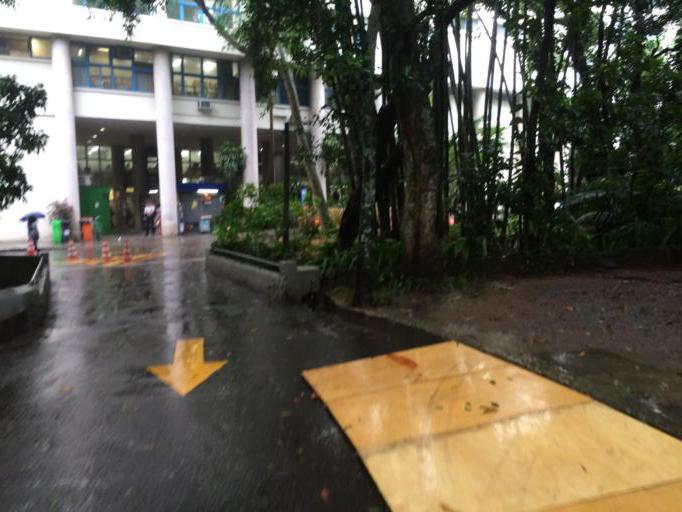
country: BR
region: Rio de Janeiro
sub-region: Rio De Janeiro
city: Rio de Janeiro
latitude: -22.9797
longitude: -43.2331
